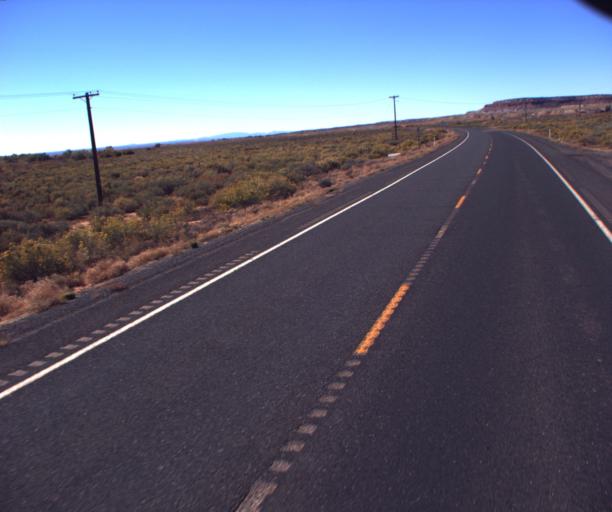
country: US
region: Arizona
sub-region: Coconino County
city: Fredonia
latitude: 36.9445
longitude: -112.5407
